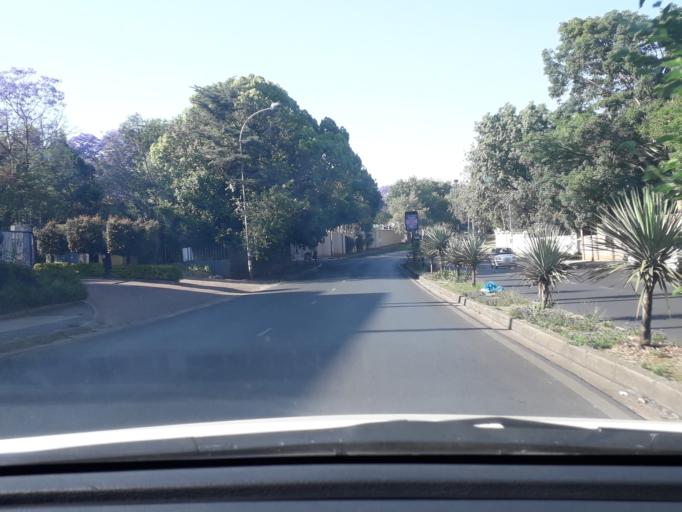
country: ZA
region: Gauteng
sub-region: City of Johannesburg Metropolitan Municipality
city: Johannesburg
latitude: -26.1323
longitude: 28.0356
